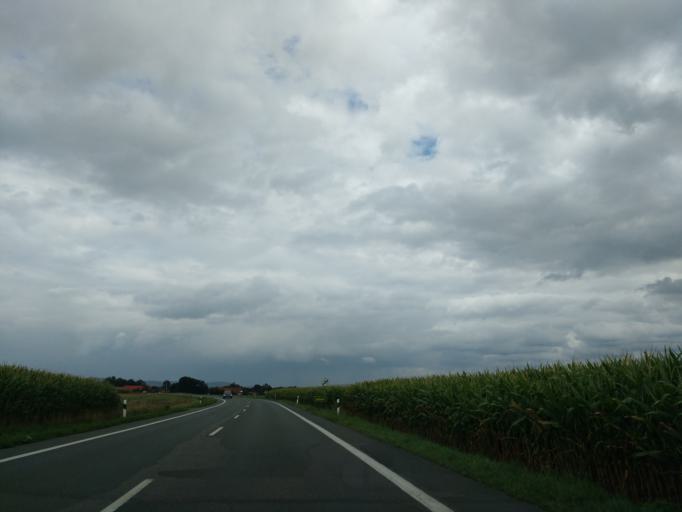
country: DE
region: Lower Saxony
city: Hilter
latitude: 52.1014
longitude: 8.1266
